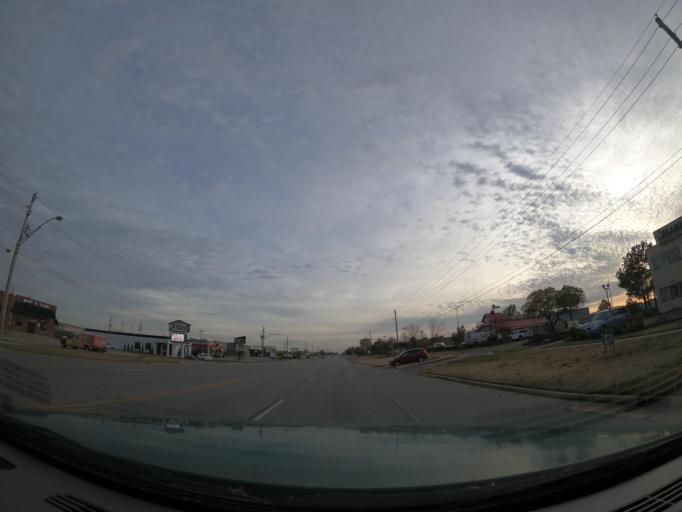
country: US
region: Oklahoma
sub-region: Tulsa County
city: Broken Arrow
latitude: 36.0595
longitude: -95.8154
